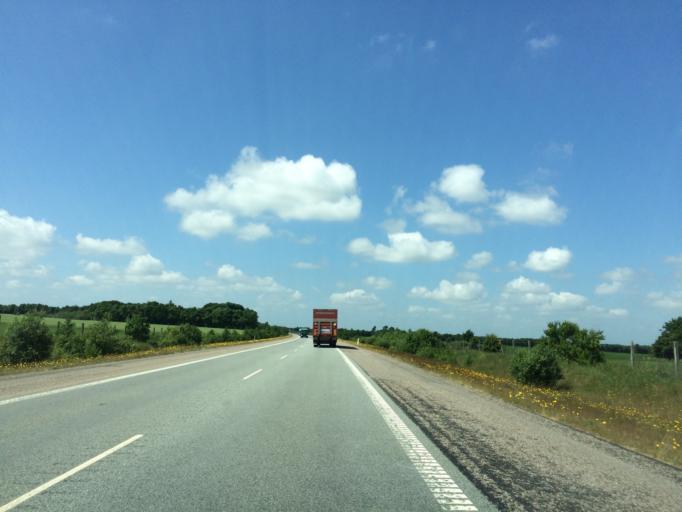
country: DK
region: Central Jutland
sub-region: Herning Kommune
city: Herning
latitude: 56.1873
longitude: 8.9430
